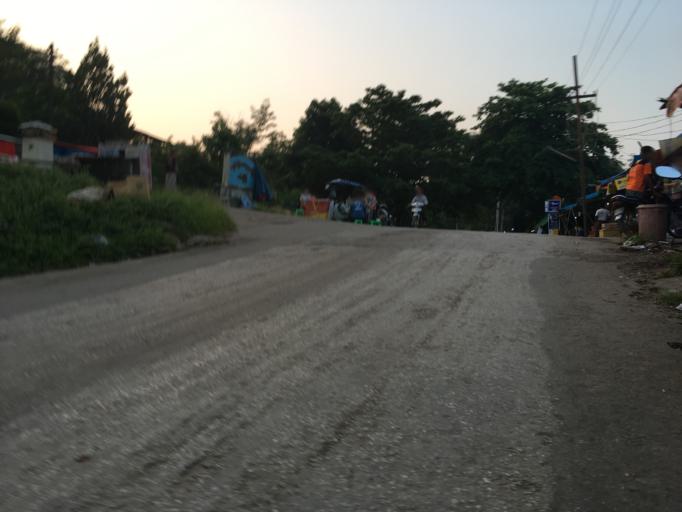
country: MM
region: Mon
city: Mawlamyine
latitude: 16.4810
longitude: 97.6263
